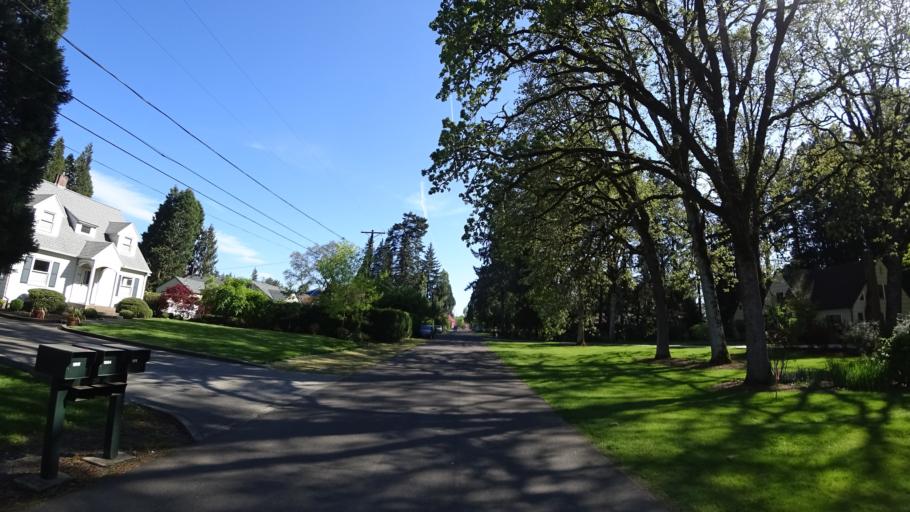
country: US
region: Oregon
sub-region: Washington County
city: Hillsboro
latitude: 45.5318
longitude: -122.9859
